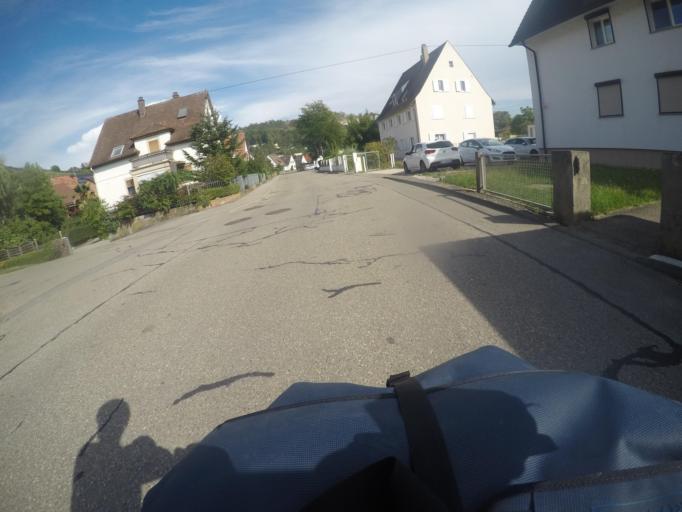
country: FR
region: Alsace
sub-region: Departement du Haut-Rhin
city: Rosenau
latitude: 47.6602
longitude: 7.5379
